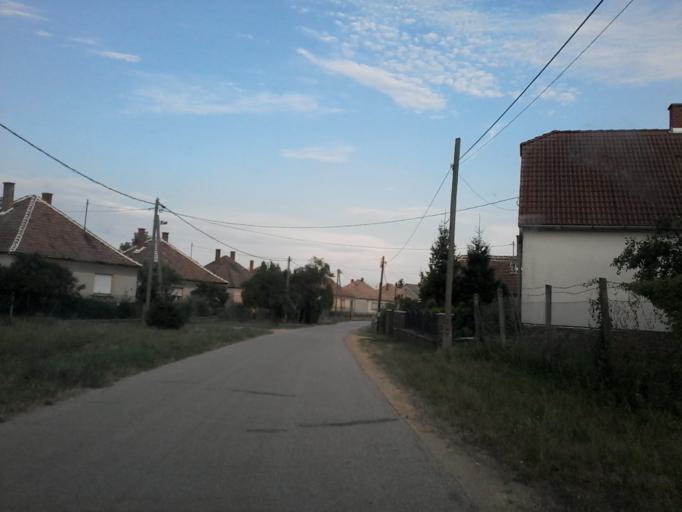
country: HU
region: Vas
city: Sarvar
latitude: 47.2081
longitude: 17.0239
